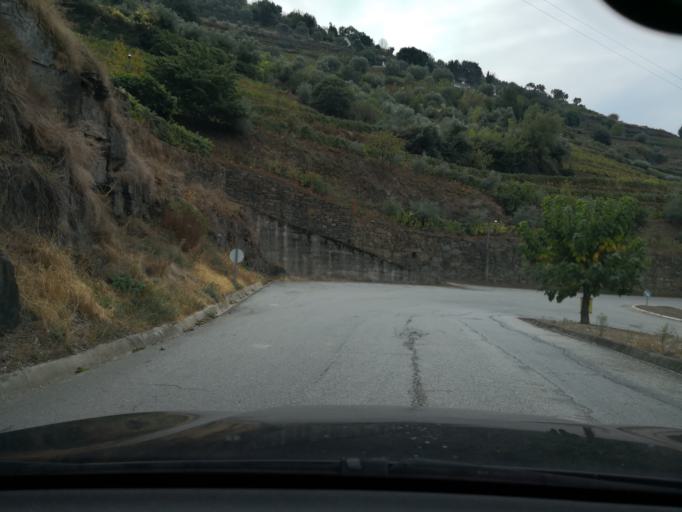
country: PT
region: Vila Real
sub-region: Peso da Regua
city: Peso da Regua
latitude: 41.1711
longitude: -7.7496
